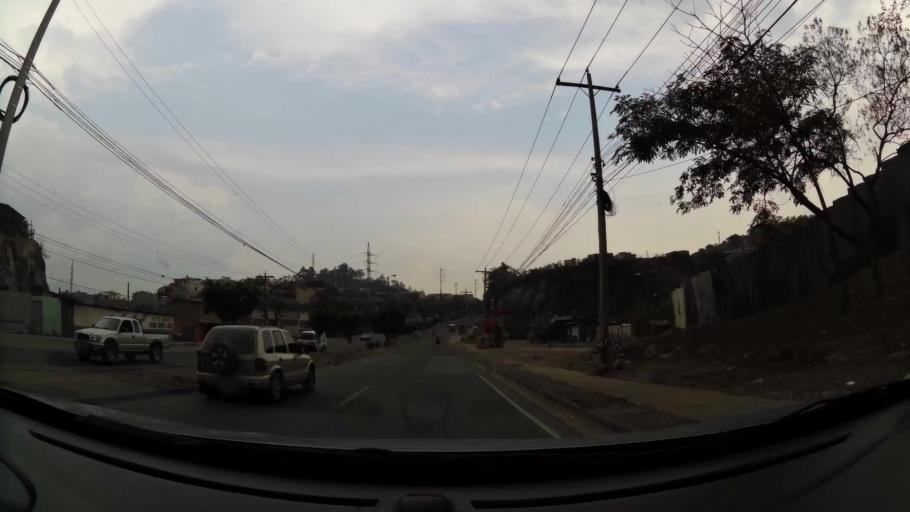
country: HN
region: Francisco Morazan
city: El Lolo
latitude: 14.0962
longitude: -87.2400
